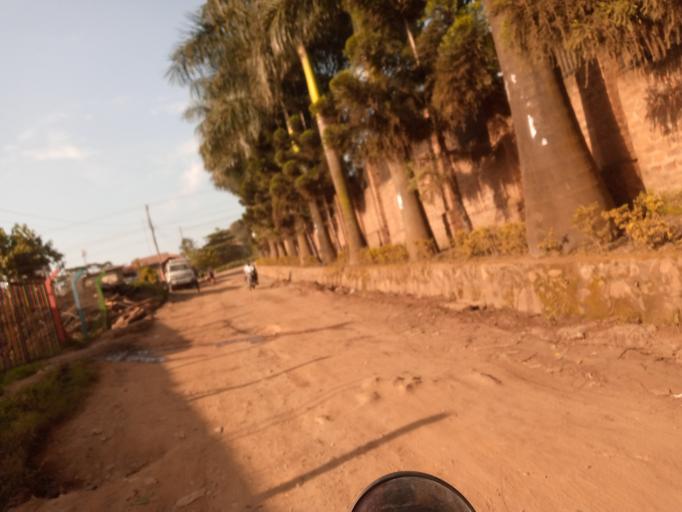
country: UG
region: Eastern Region
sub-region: Mbale District
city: Mbale
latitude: 1.0675
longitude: 34.1769
